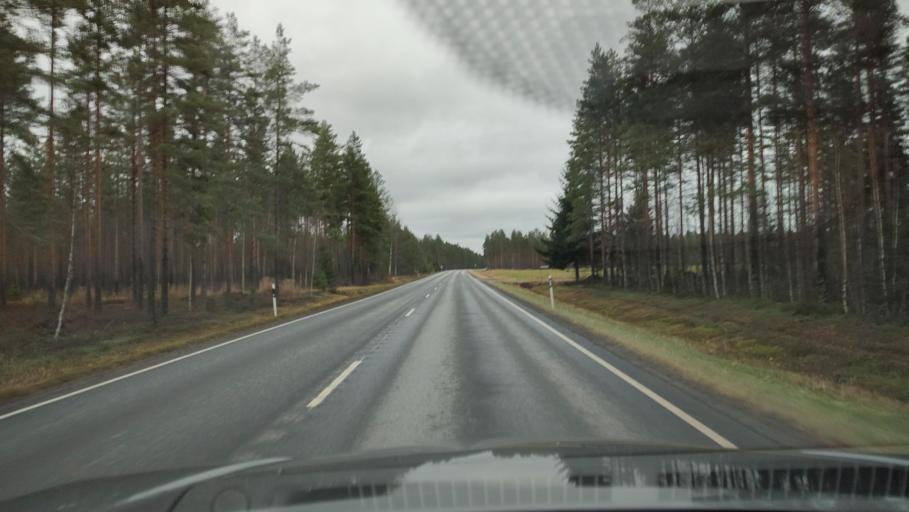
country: FI
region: Southern Ostrobothnia
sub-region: Seinaejoki
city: Kurikka
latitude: 62.5128
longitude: 22.3111
